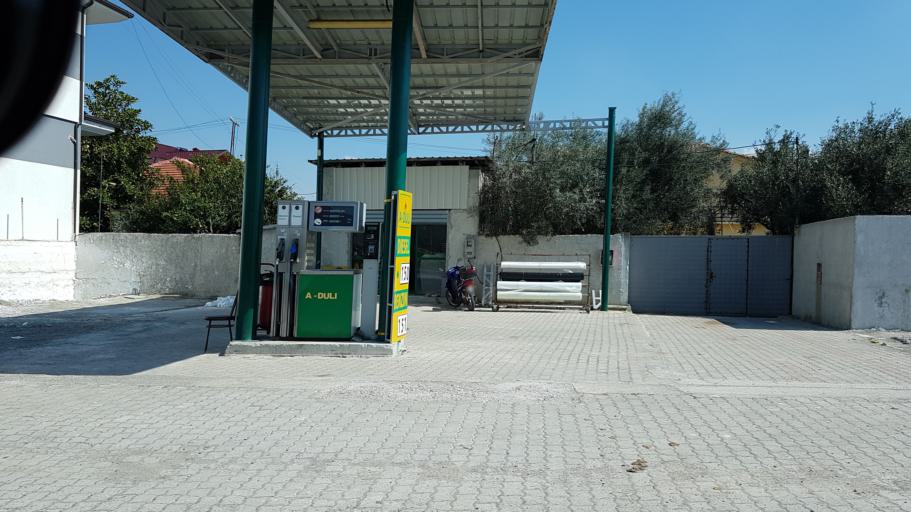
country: AL
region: Shkoder
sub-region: Rrethi i Shkodres
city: Vau i Dejes
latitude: 41.9984
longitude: 19.6157
